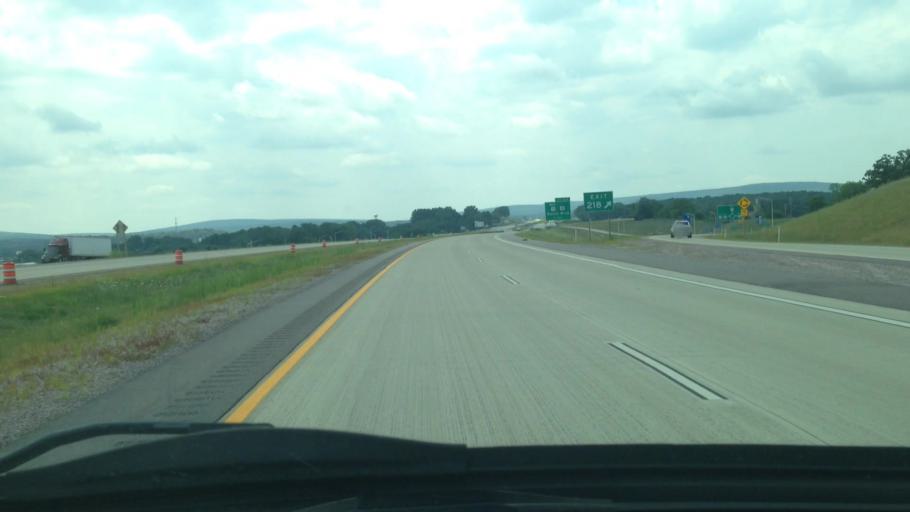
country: US
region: Wisconsin
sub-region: Sauk County
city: West Baraboo
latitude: 43.4787
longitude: -89.7746
